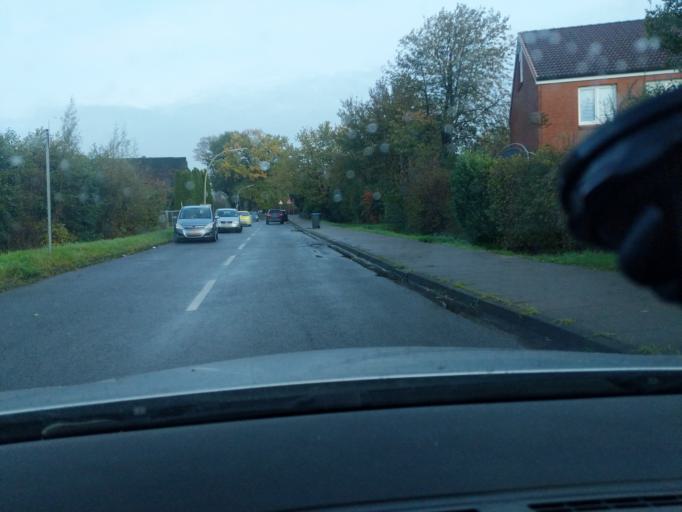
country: DE
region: Lower Saxony
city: Neu Wulmstorf
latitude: 53.5223
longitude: 9.7792
